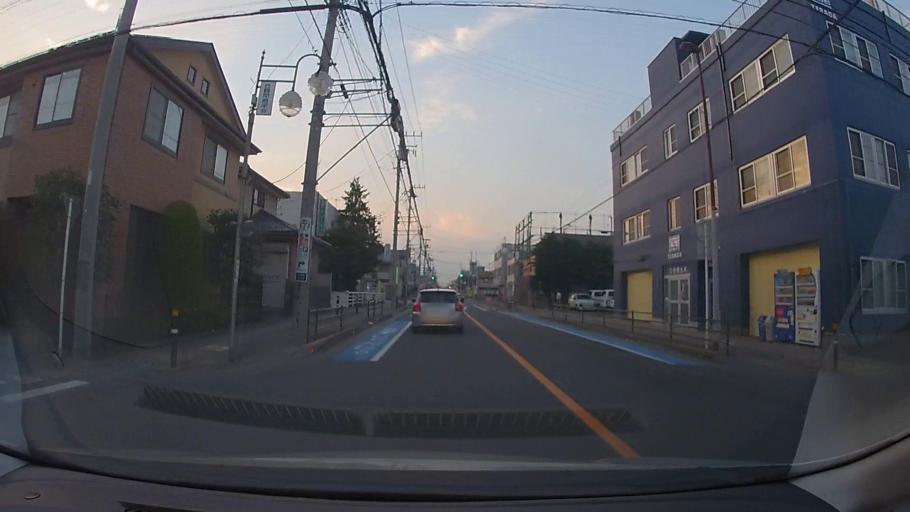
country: JP
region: Kanagawa
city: Minami-rinkan
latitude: 35.4834
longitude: 139.4508
